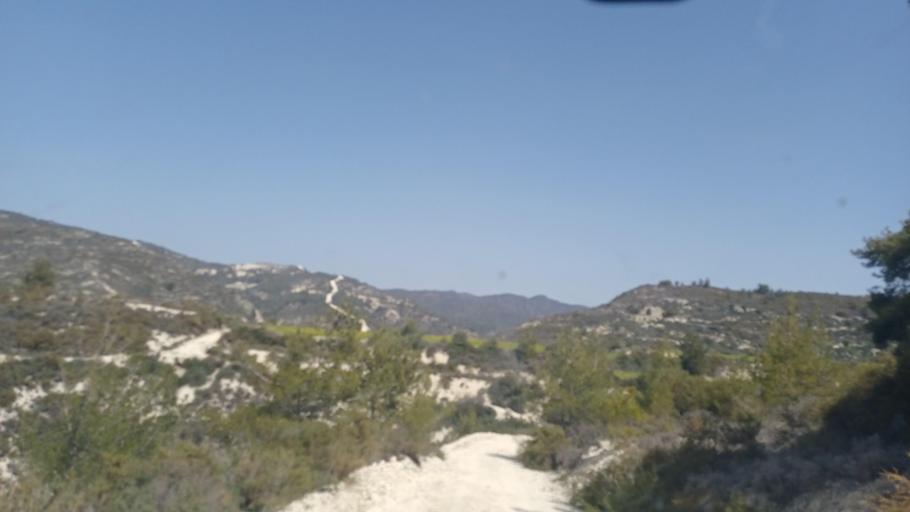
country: CY
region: Limassol
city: Pachna
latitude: 34.8600
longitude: 32.7353
